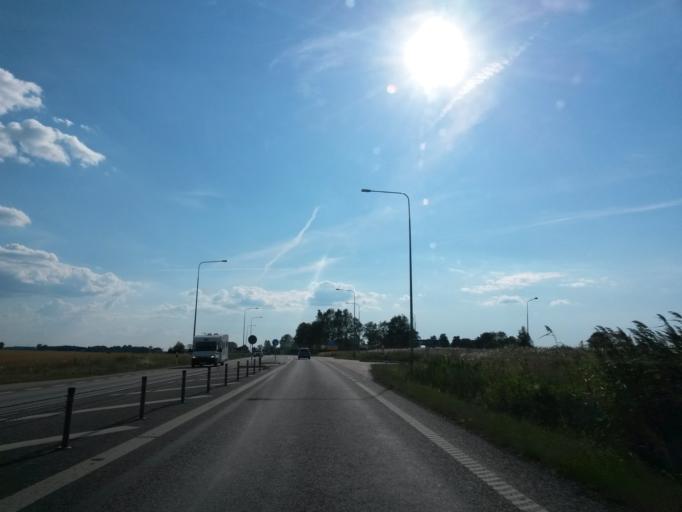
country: SE
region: Vaestra Goetaland
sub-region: Vara Kommun
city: Vara
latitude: 58.2919
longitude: 13.0429
